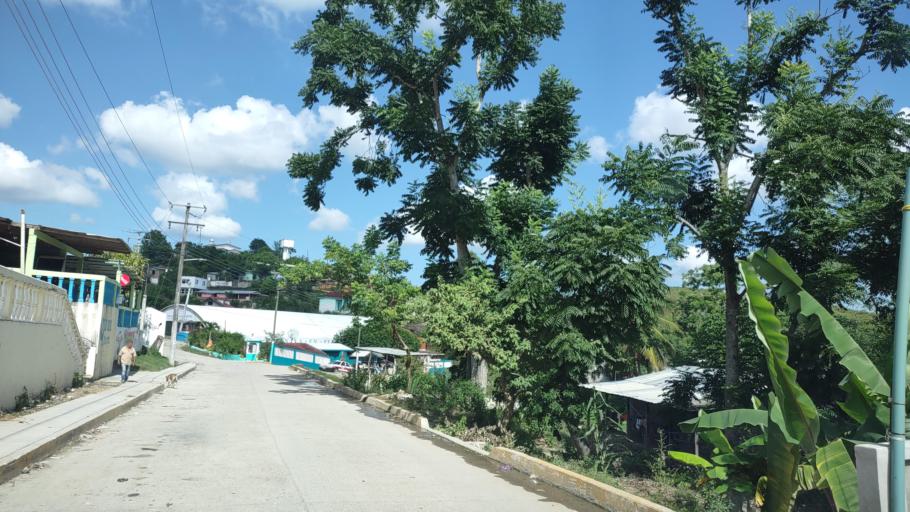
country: MM
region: Shan
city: Taunggyi
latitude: 20.5837
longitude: 97.3759
